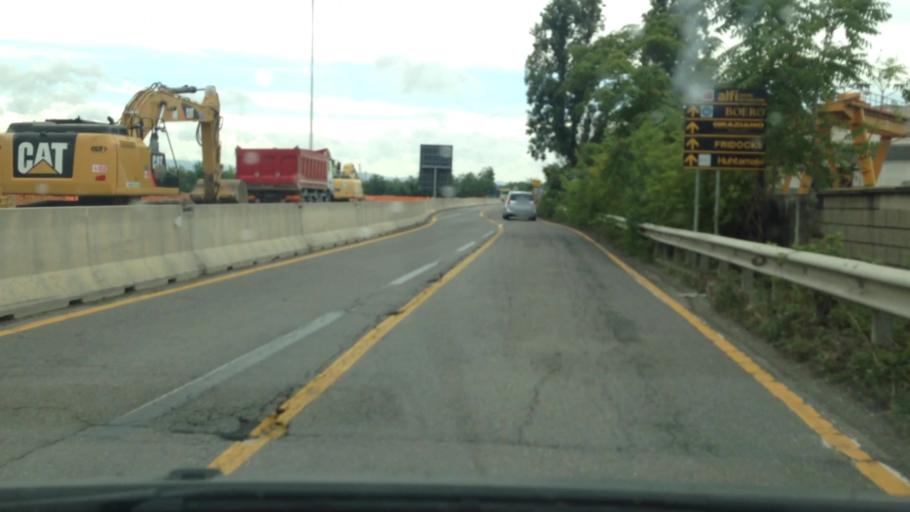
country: IT
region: Piedmont
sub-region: Provincia di Alessandria
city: Tortona
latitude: 44.9047
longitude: 8.8375
